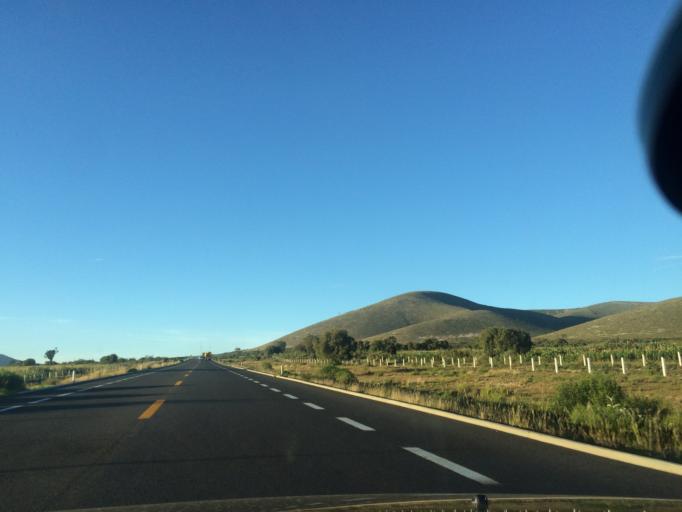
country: MX
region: Puebla
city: Morelos Canada
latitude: 18.7374
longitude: -97.4767
